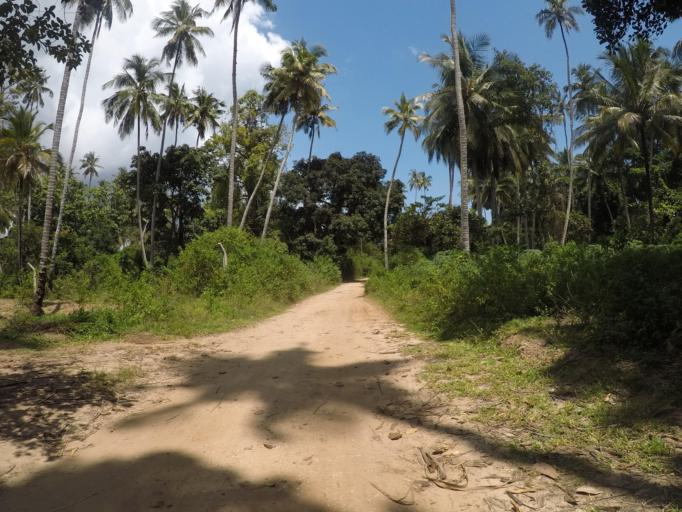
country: TZ
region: Zanzibar North
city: Mkokotoni
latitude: -5.9913
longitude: 39.1868
